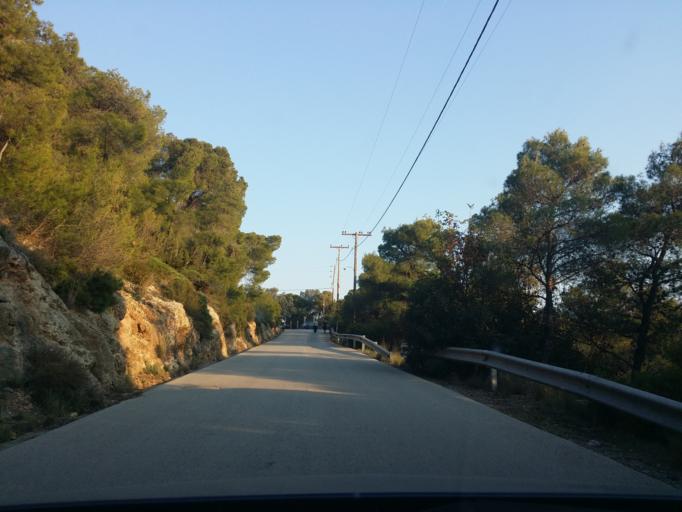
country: GR
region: Attica
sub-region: Nomos Piraios
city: Poros
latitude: 37.5052
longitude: 23.4767
